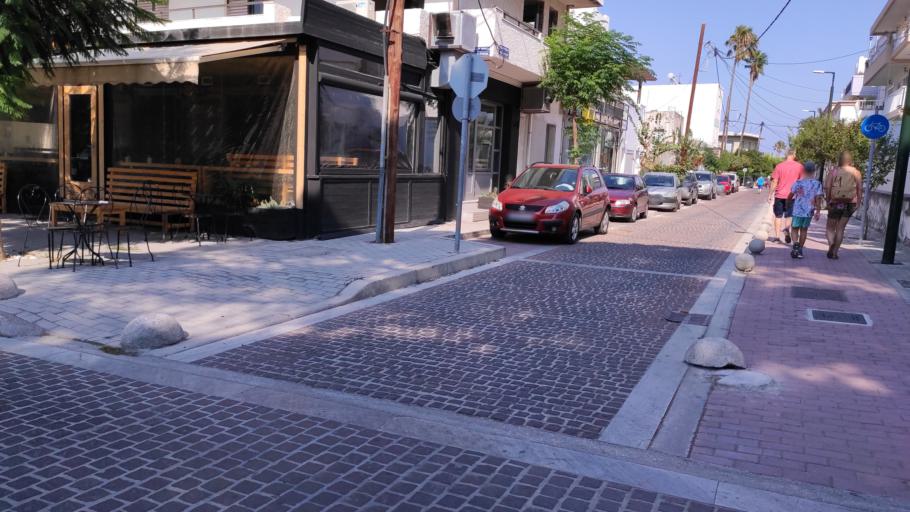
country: GR
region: South Aegean
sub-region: Nomos Dodekanisou
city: Kos
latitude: 36.8914
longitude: 27.2903
